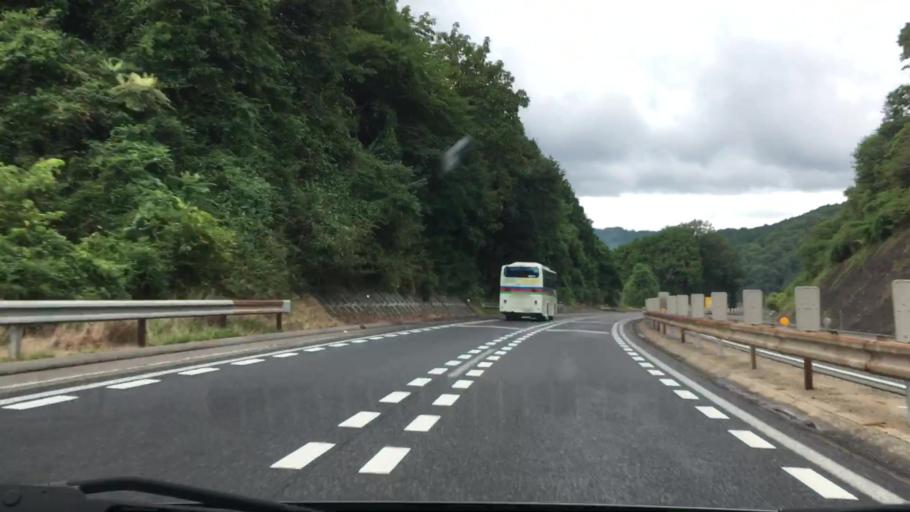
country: JP
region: Okayama
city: Takahashi
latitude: 34.9904
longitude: 133.7209
